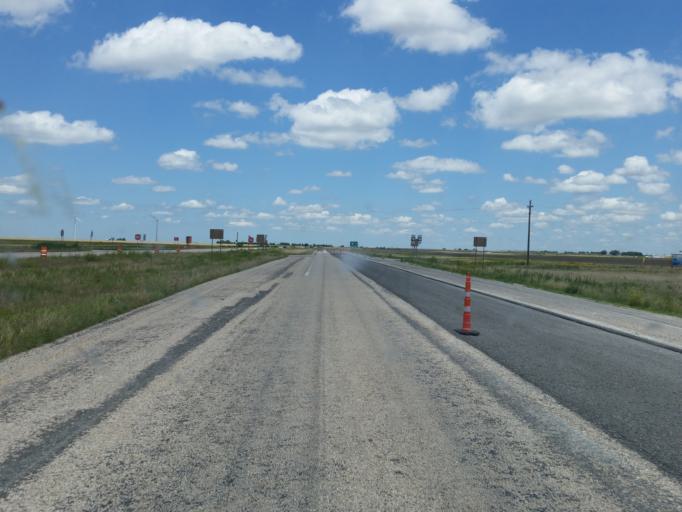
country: US
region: Texas
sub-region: Nolan County
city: Roscoe
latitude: 32.4549
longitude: -100.5419
